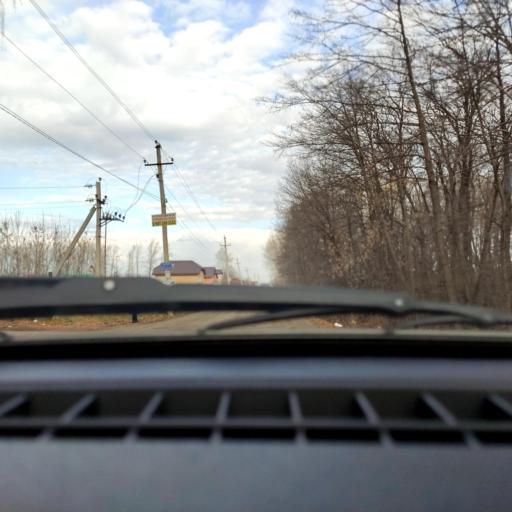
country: RU
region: Bashkortostan
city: Ufa
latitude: 54.6287
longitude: 55.8902
